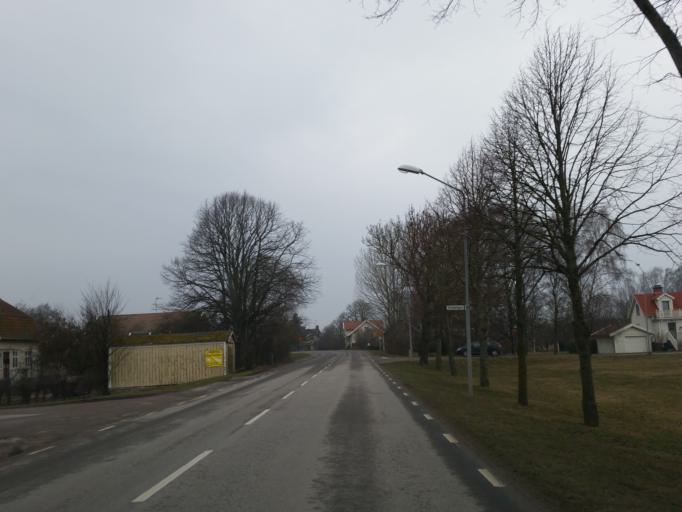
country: SE
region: Kalmar
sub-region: Morbylanga Kommun
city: Moerbylanga
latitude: 56.5247
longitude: 16.3931
